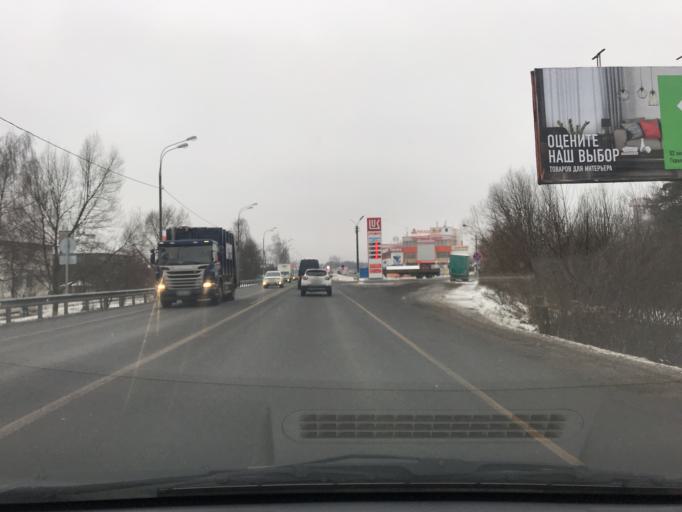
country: RU
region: Moskovskaya
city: Elektrostal'
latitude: 55.8101
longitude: 38.4268
